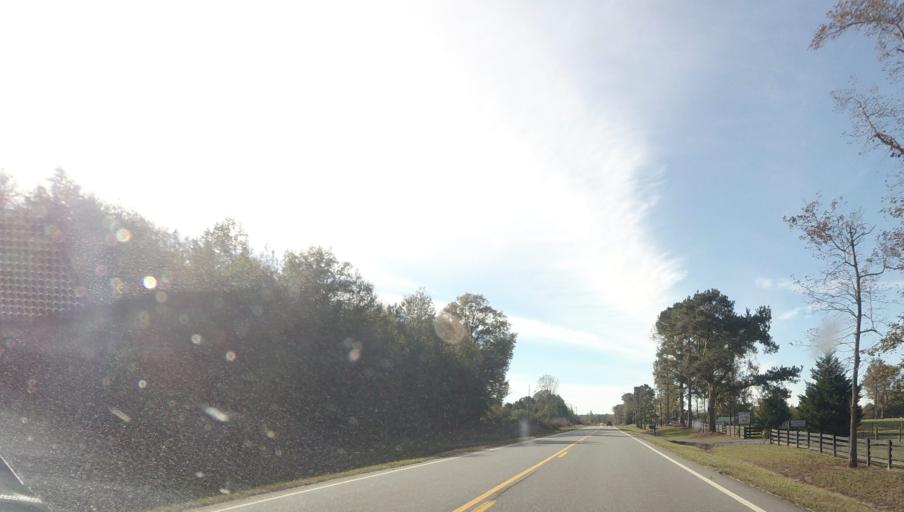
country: US
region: Georgia
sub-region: Upson County
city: Thomaston
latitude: 32.7207
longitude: -84.3177
